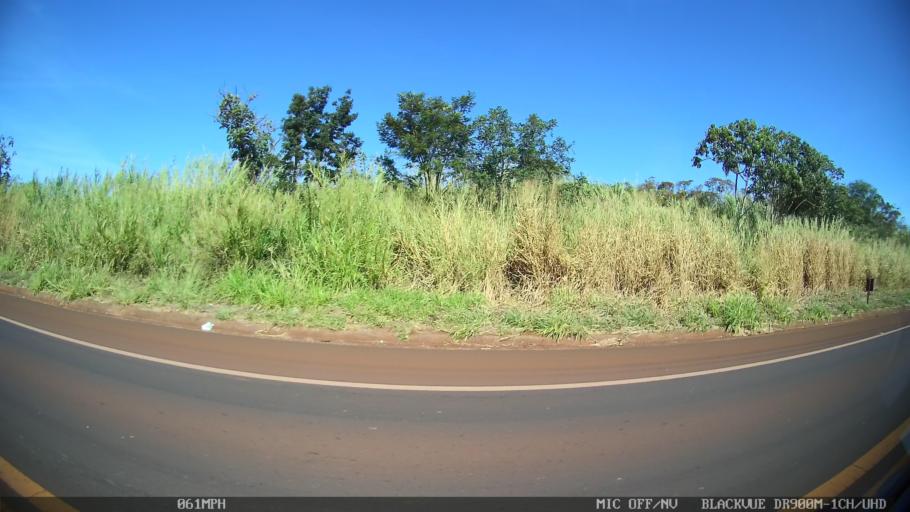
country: BR
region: Sao Paulo
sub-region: Ipua
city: Ipua
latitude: -20.4930
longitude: -48.0180
